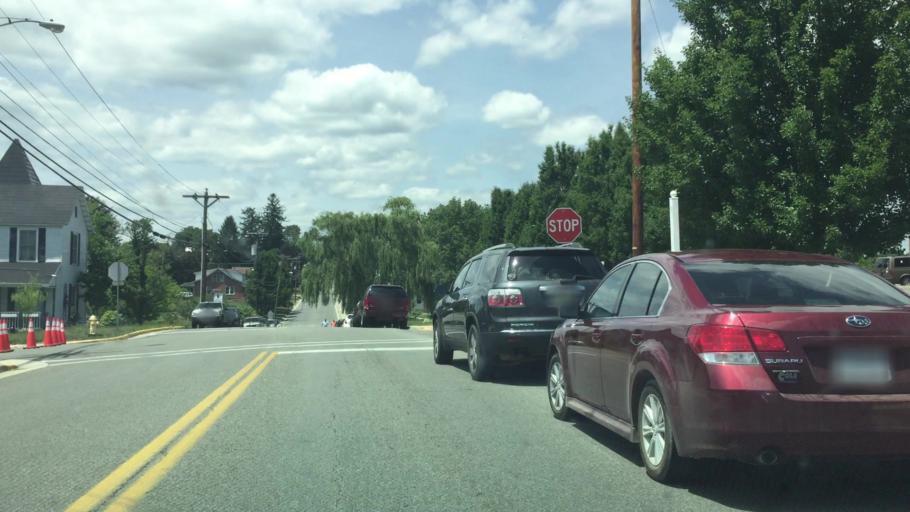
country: US
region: Virginia
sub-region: Wythe County
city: Wytheville
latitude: 36.9516
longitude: -81.0855
